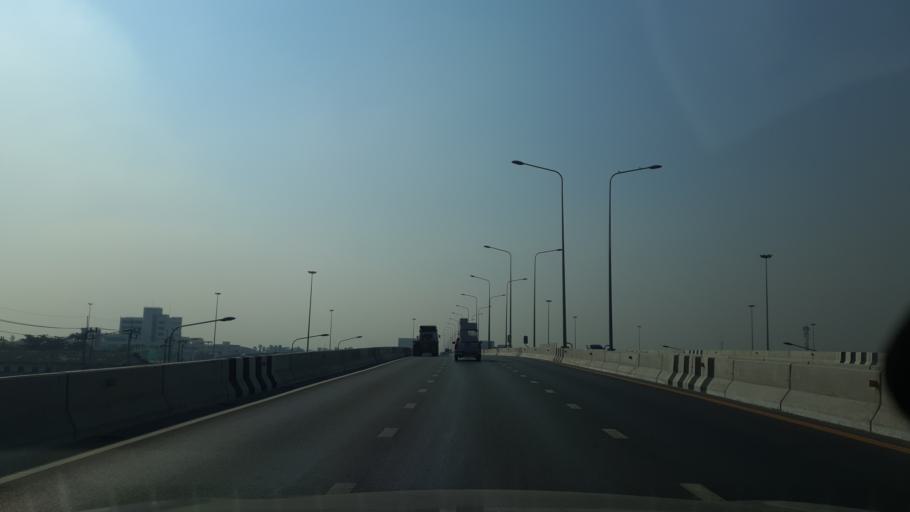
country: TH
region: Nonthaburi
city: Bang Bua Thong
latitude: 13.9539
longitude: 100.4584
